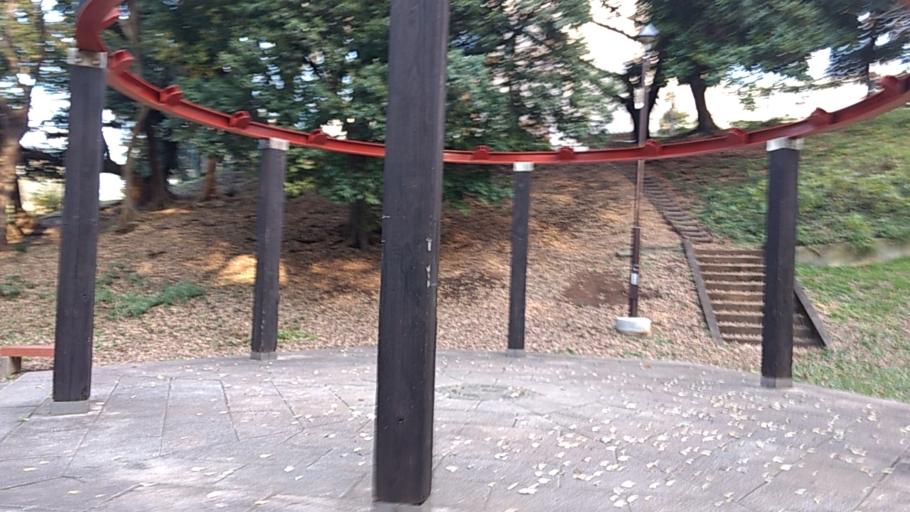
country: JP
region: Tokyo
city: Tokyo
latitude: 35.7040
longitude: 139.7140
